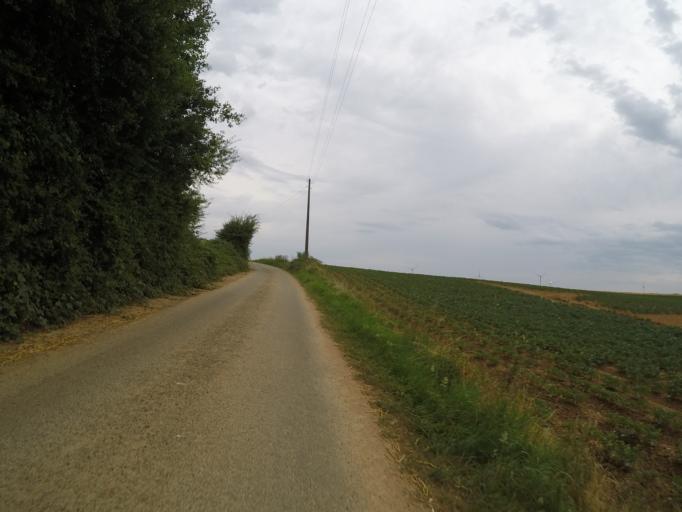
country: BE
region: Wallonia
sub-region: Province de Namur
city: Assesse
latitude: 50.3115
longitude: 5.0049
